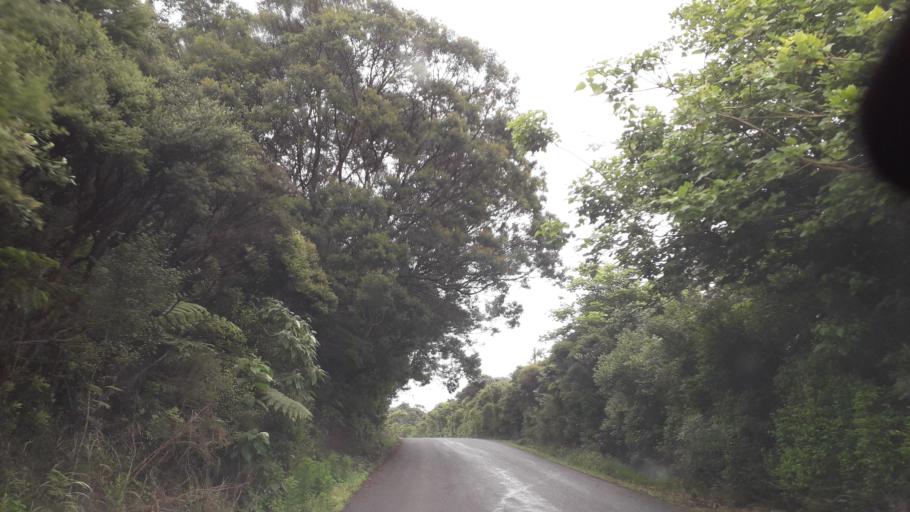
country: NZ
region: Northland
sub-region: Far North District
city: Paihia
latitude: -35.2290
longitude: 174.2622
